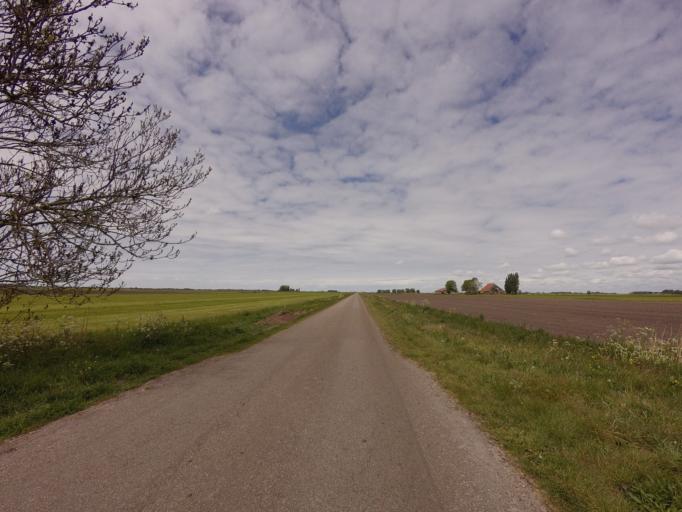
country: NL
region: Friesland
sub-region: Gemeente Gaasterlan-Sleat
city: Oudemirdum
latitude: 52.9001
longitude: 5.5093
